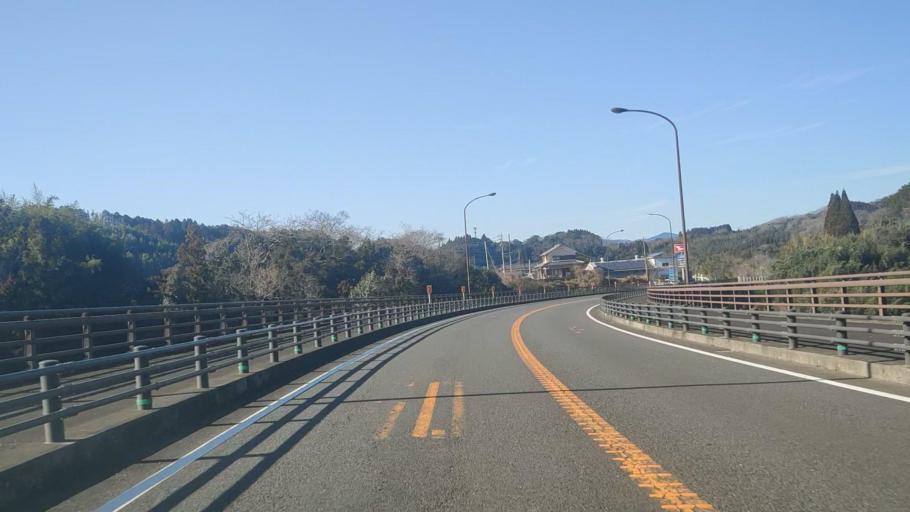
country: JP
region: Oita
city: Usuki
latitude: 33.0579
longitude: 131.6745
